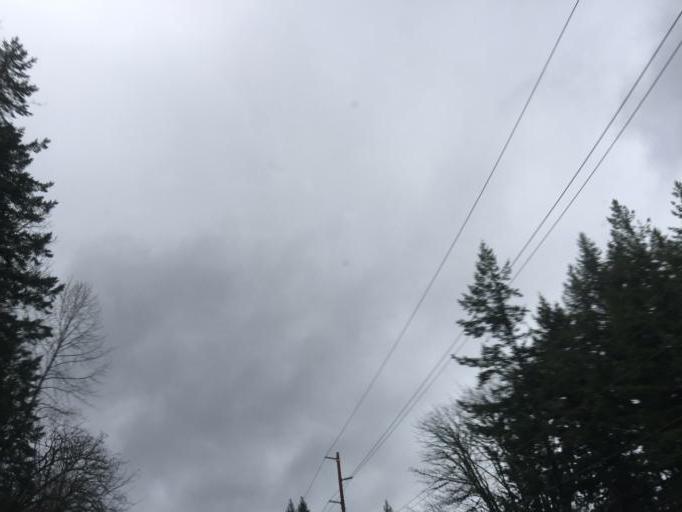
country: US
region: Washington
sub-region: King County
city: Snoqualmie
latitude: 47.5156
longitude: -121.8344
